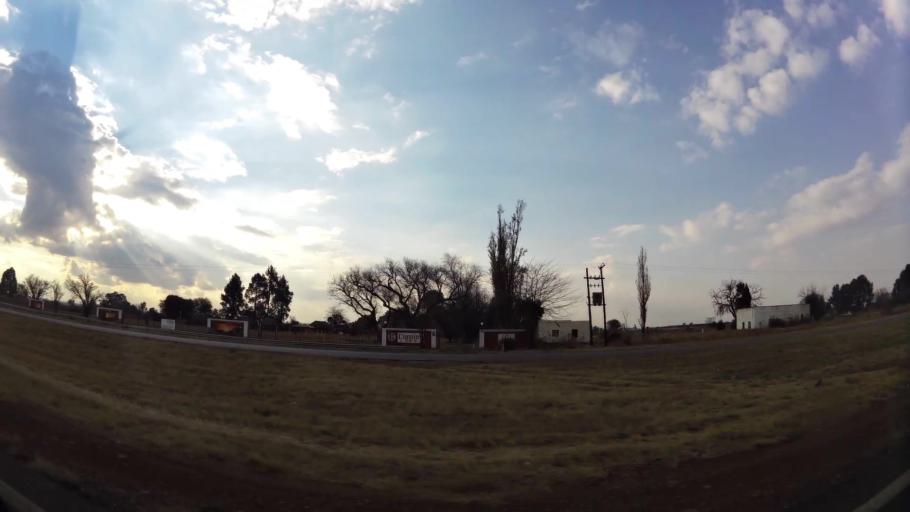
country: ZA
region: Gauteng
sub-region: Sedibeng District Municipality
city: Vanderbijlpark
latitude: -26.6192
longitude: 27.8250
